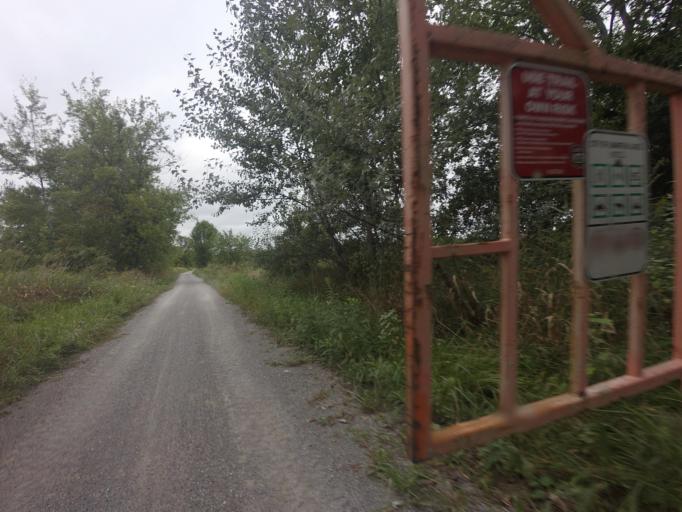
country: CA
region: Ontario
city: Omemee
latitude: 44.4413
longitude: -78.7700
